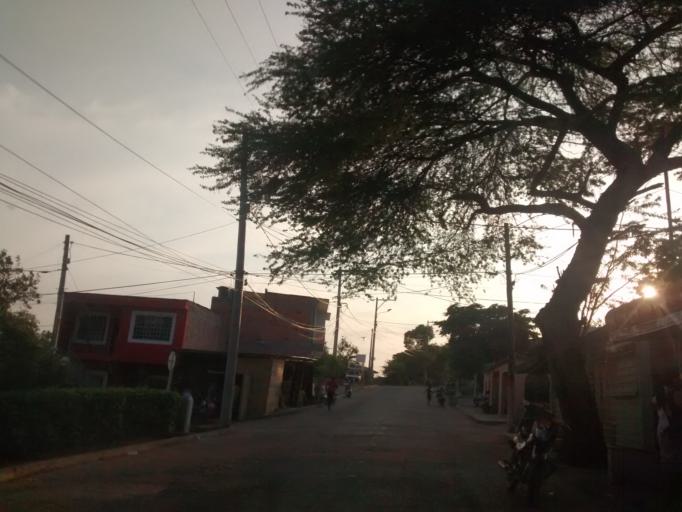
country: CO
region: Cundinamarca
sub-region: Girardot
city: Girardot City
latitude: 4.3219
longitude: -74.7860
